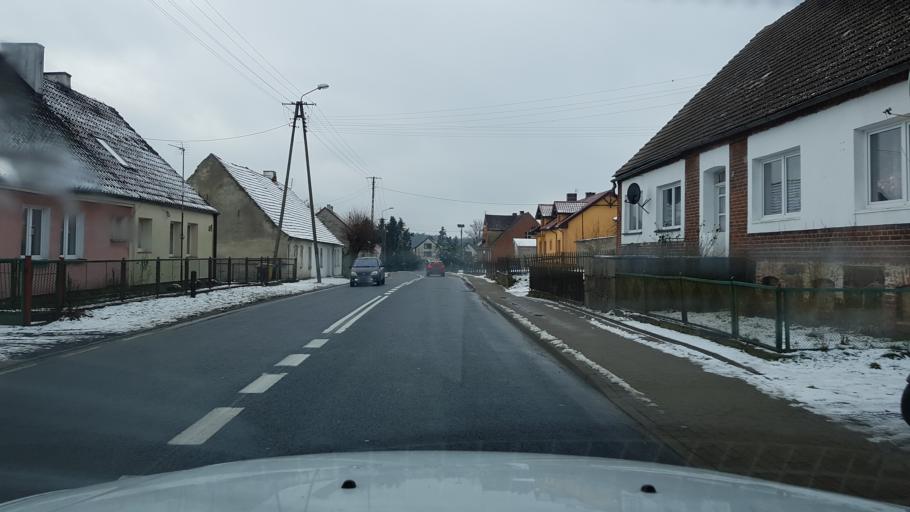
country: PL
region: West Pomeranian Voivodeship
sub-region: Powiat drawski
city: Wierzchowo
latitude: 53.5545
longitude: 16.1306
